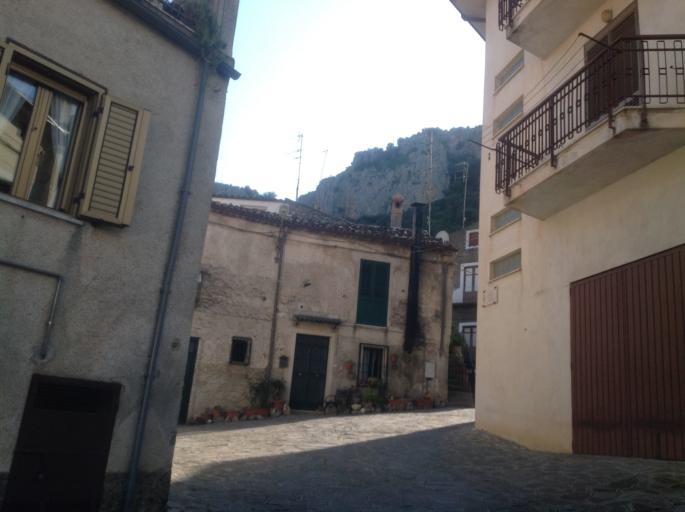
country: IT
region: Calabria
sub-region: Provincia di Cosenza
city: Civita
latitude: 39.8281
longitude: 16.3142
